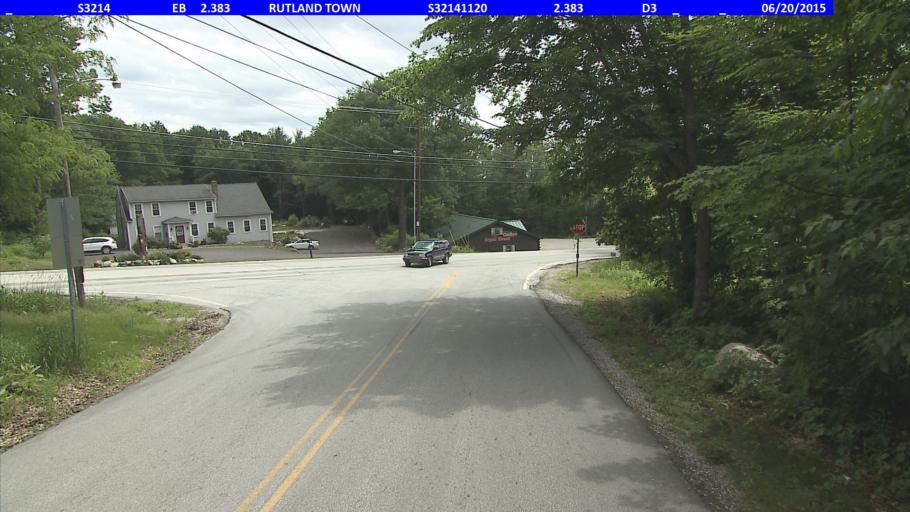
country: US
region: Vermont
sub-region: Rutland County
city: Rutland
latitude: 43.6311
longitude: -72.9435
